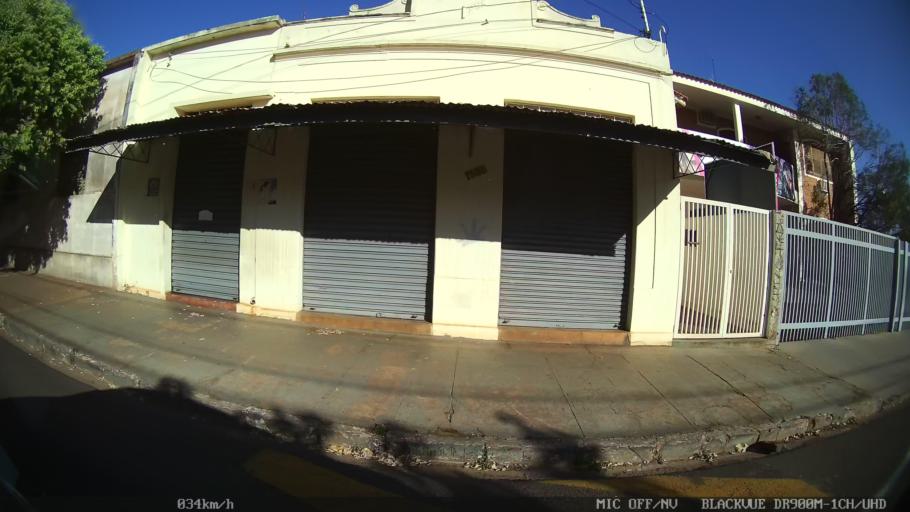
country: BR
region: Sao Paulo
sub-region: Olimpia
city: Olimpia
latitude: -20.7396
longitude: -48.9189
